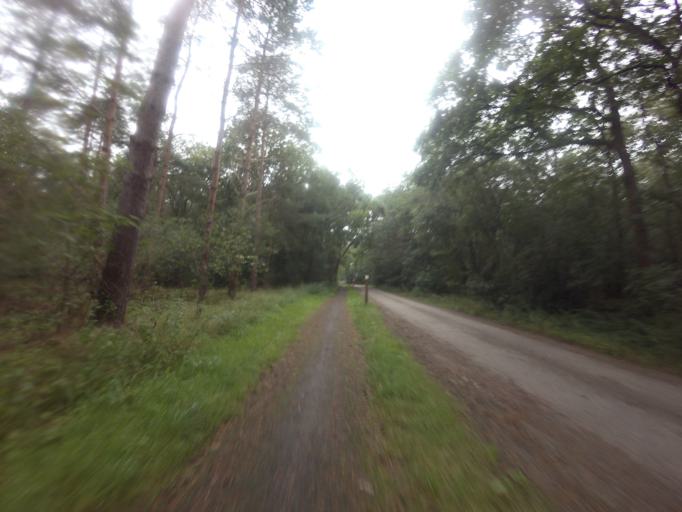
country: NL
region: Friesland
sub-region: Gemeente Heerenveen
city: Nieuwehorne
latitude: 52.9523
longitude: 6.1027
